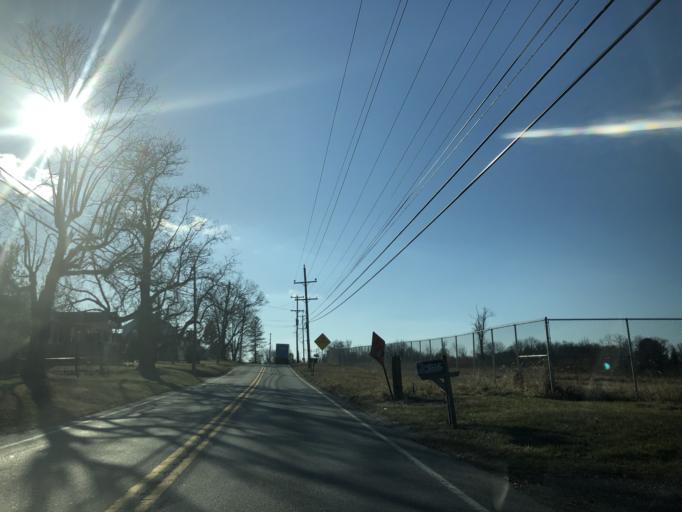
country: US
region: Pennsylvania
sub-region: Chester County
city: South Coatesville
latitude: 39.9645
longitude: -75.8371
